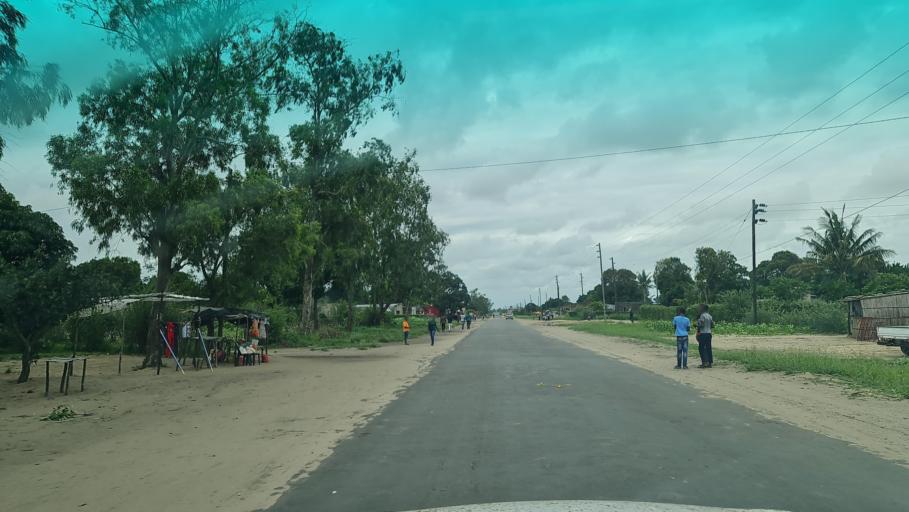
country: MZ
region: Maputo
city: Manhica
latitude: -25.4425
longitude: 32.7736
